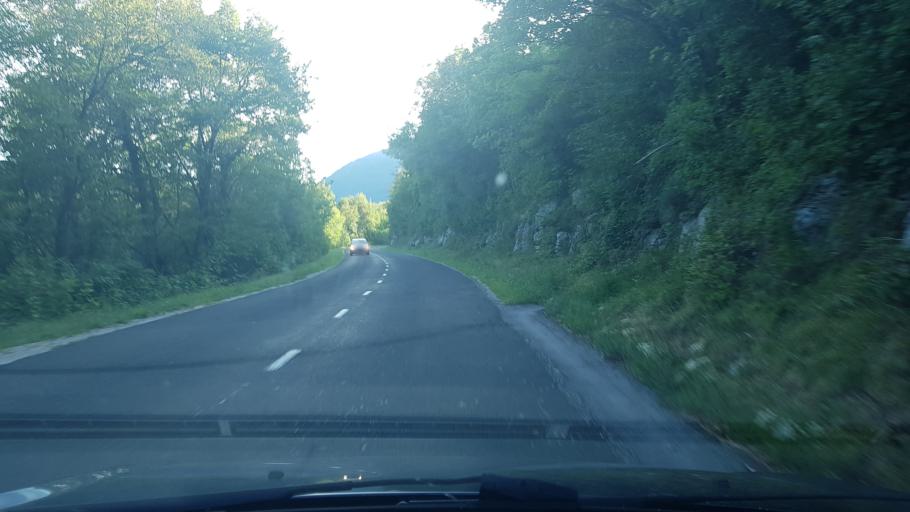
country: SI
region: Nova Gorica
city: Solkan
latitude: 46.0144
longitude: 13.6848
